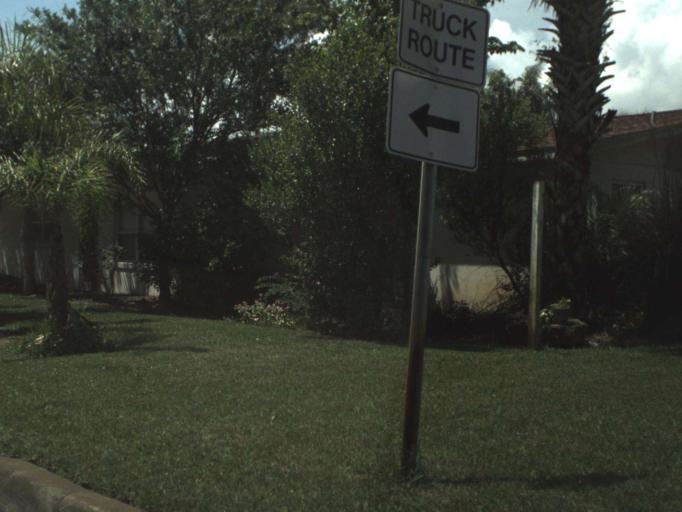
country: US
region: Florida
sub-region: Volusia County
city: Port Orange
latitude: 29.1510
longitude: -80.9718
